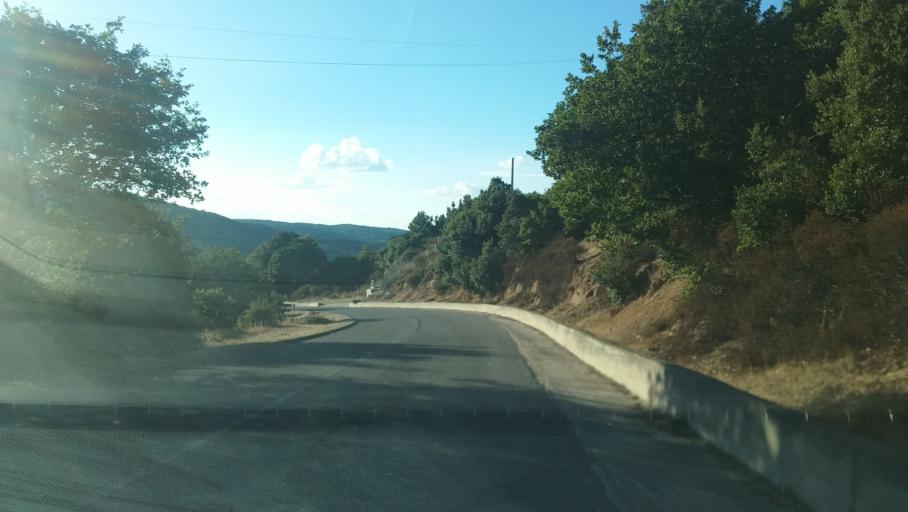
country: IT
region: Sardinia
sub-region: Provincia di Nuoro
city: Orgosolo
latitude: 40.1999
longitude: 9.3497
